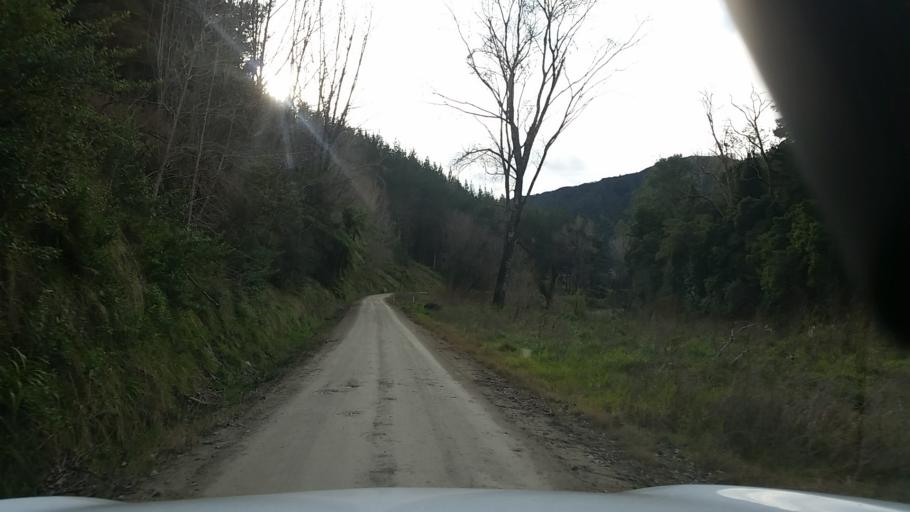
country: NZ
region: Taranaki
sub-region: South Taranaki District
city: Patea
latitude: -39.5788
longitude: 174.8259
